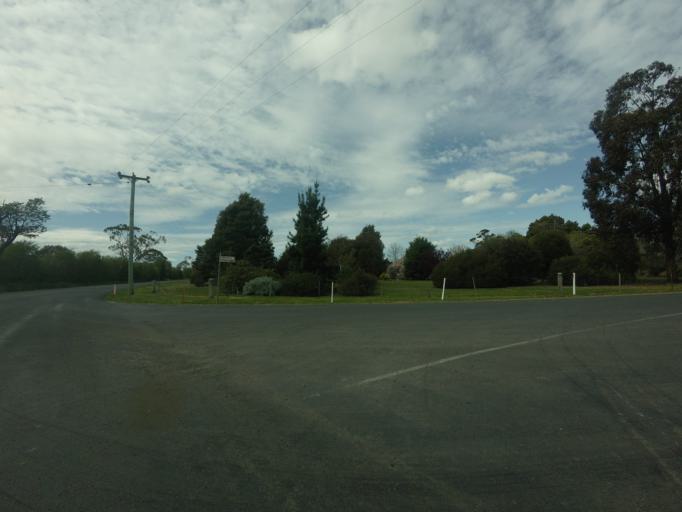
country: AU
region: Tasmania
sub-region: Northern Midlands
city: Longford
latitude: -41.6270
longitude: 147.1568
